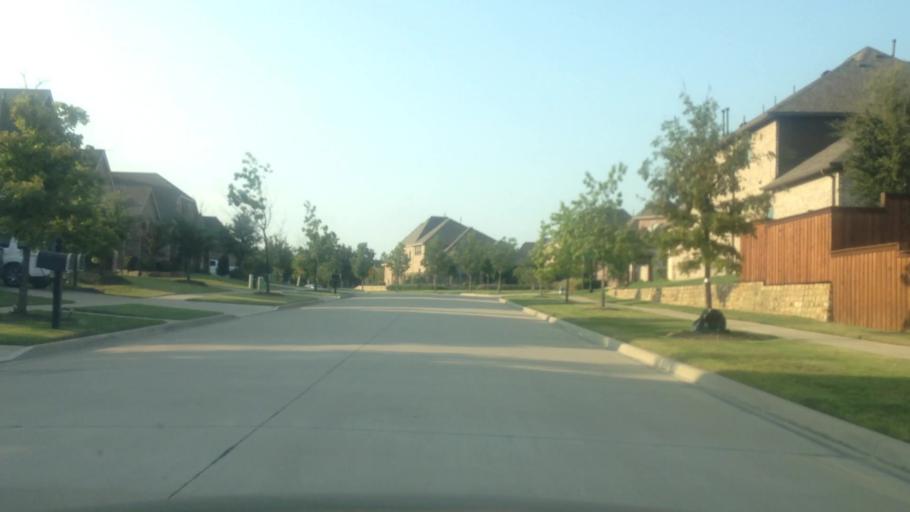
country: US
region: Texas
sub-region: Denton County
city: The Colony
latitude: 33.1300
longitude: -96.8783
